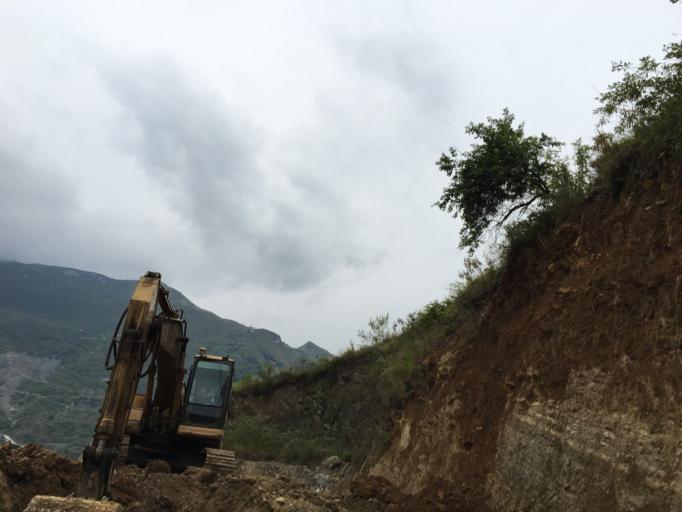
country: CN
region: Guizhou Sheng
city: Anshun
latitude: 25.9614
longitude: 105.2433
